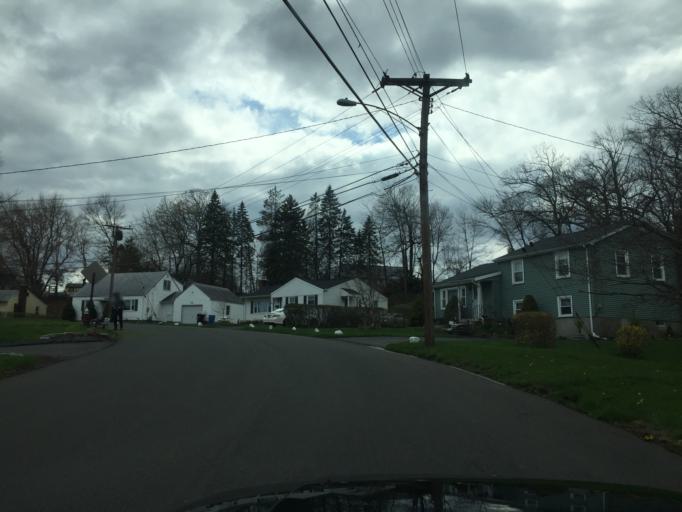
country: US
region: Connecticut
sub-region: Hartford County
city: Farmington
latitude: 41.7030
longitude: -72.7929
